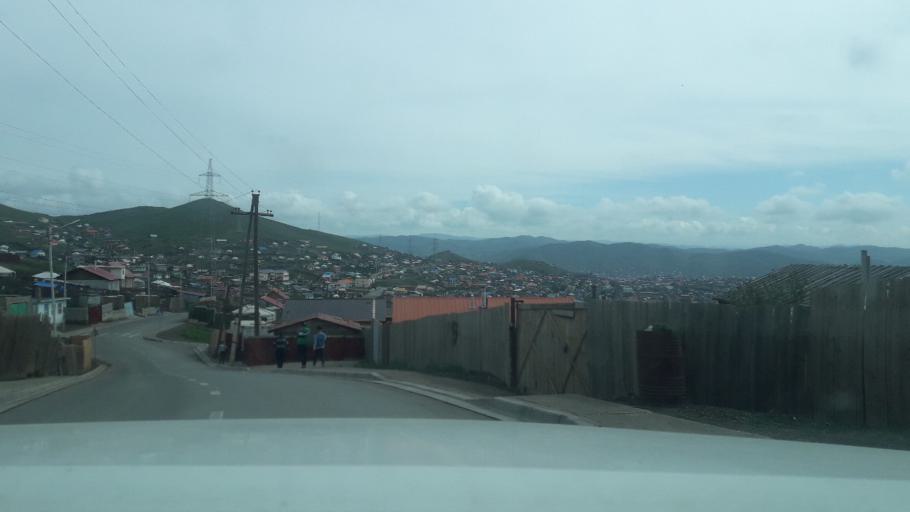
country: MN
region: Ulaanbaatar
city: Ulaanbaatar
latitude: 47.9656
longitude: 106.8802
